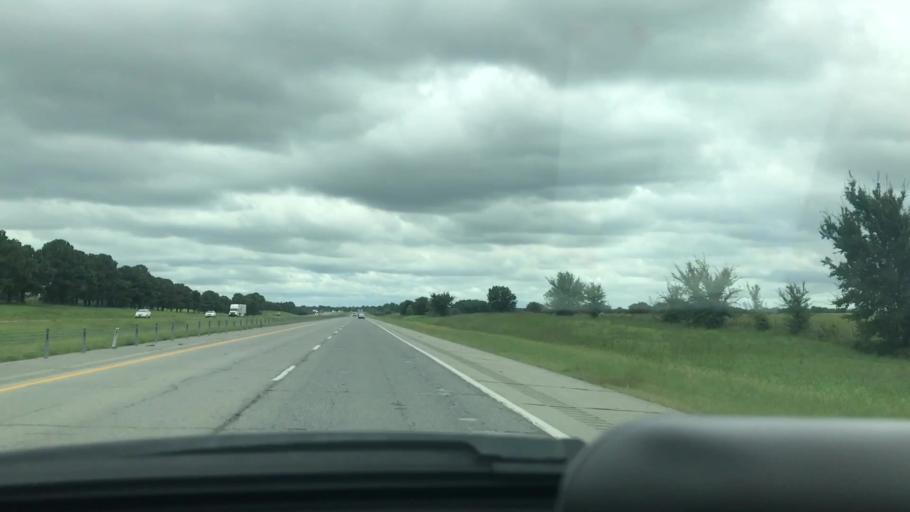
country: US
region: Oklahoma
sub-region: McIntosh County
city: Checotah
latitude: 35.5416
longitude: -95.5034
